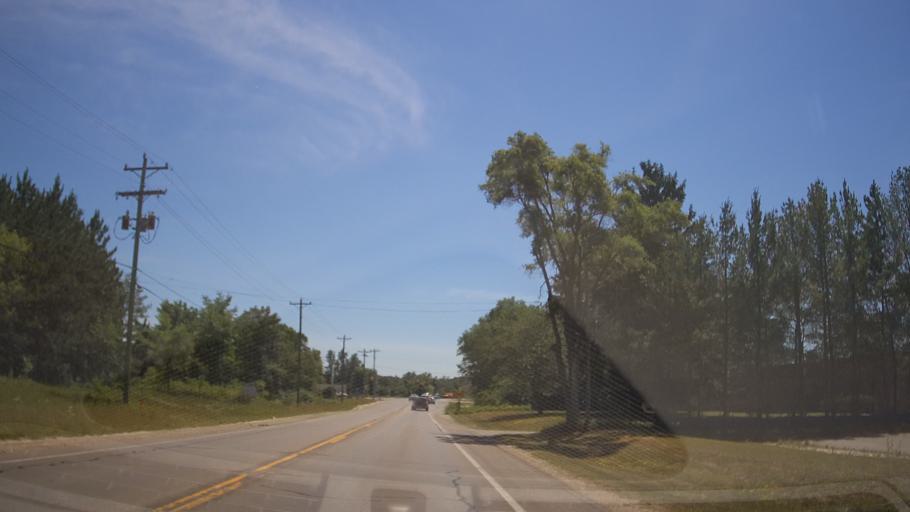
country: US
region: Michigan
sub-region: Grand Traverse County
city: Traverse City
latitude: 44.6672
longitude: -85.6902
